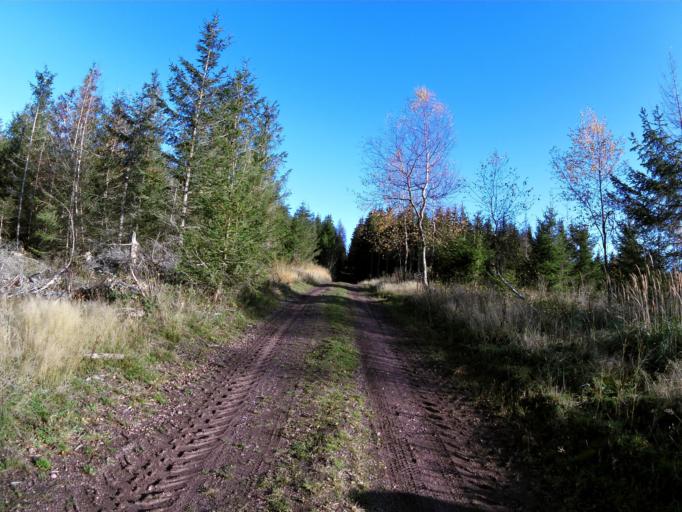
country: DE
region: Thuringia
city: Ruhla
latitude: 50.9057
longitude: 10.3514
